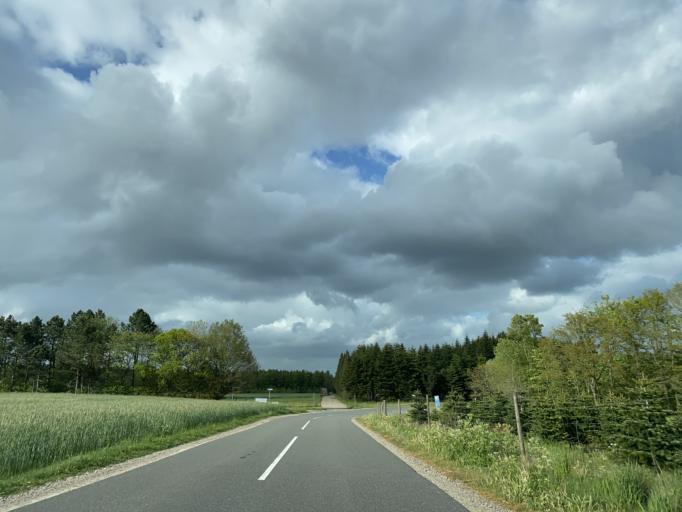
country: DK
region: Central Jutland
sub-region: Horsens Kommune
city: Braedstrup
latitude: 56.0401
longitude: 9.6641
